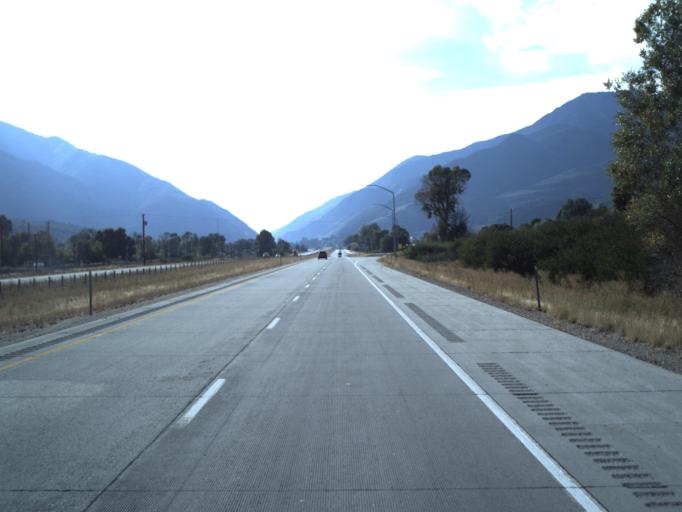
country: US
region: Utah
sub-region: Morgan County
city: Mountain Green
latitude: 41.1371
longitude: -111.7914
